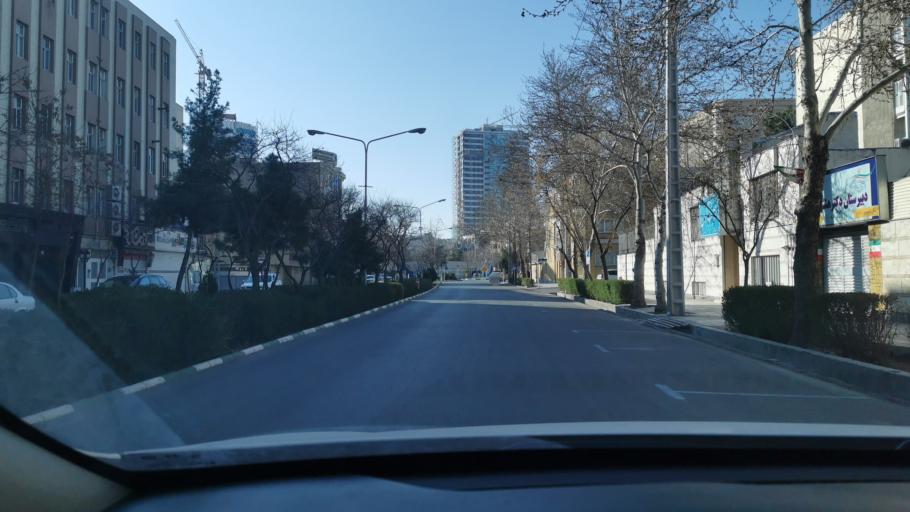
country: IR
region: Razavi Khorasan
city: Mashhad
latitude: 36.2877
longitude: 59.5673
